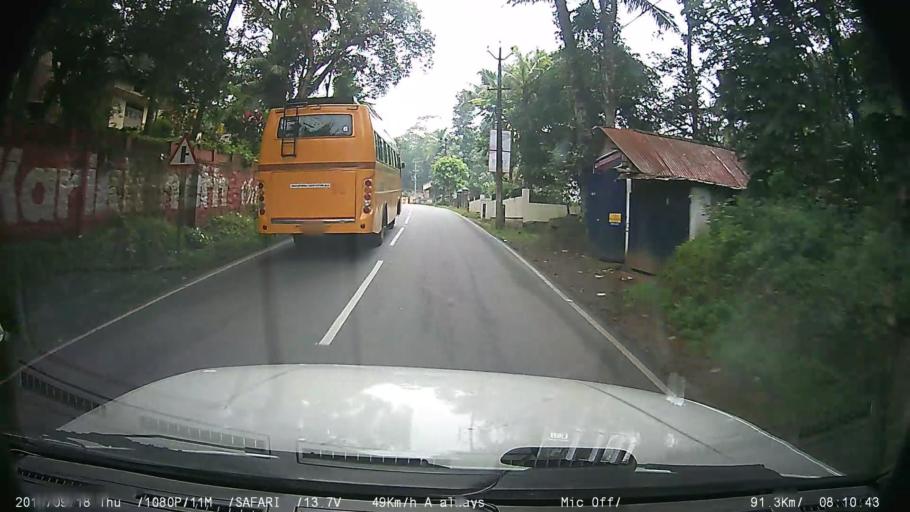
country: IN
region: Kerala
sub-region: Kottayam
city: Kottayam
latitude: 9.6038
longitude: 76.5928
